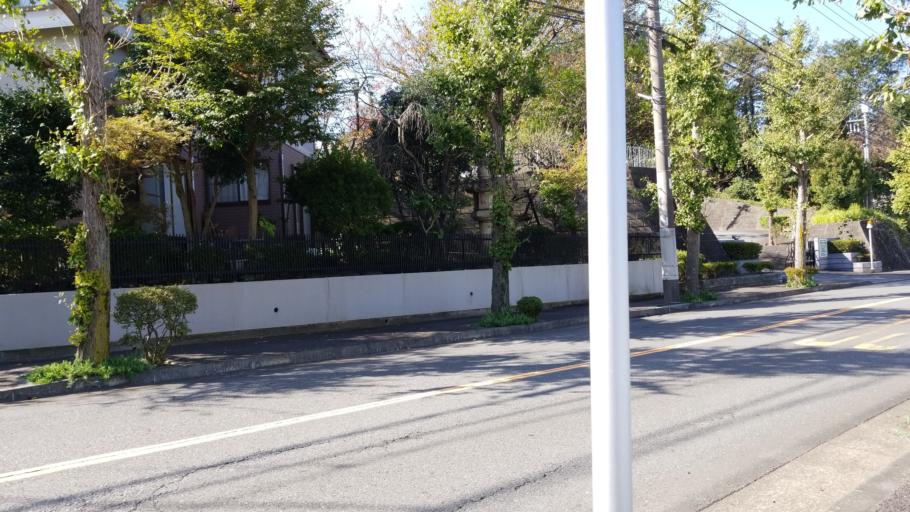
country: JP
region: Tokyo
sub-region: Machida-shi
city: Machida
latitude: 35.5913
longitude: 139.5017
